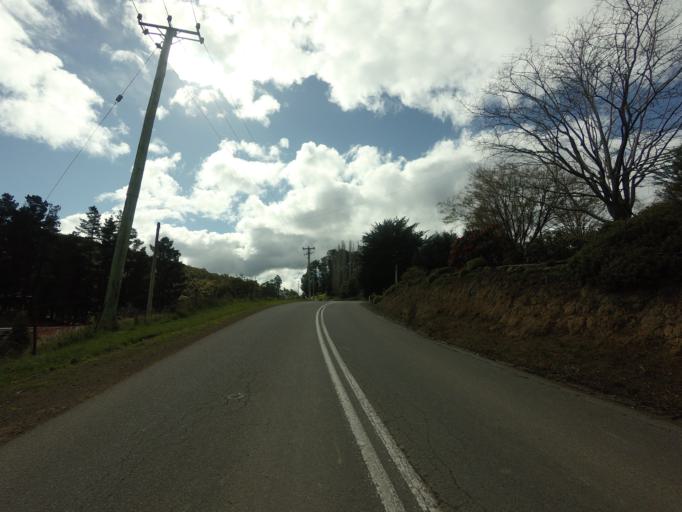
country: AU
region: Tasmania
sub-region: Huon Valley
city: Geeveston
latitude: -43.2390
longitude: 146.9916
